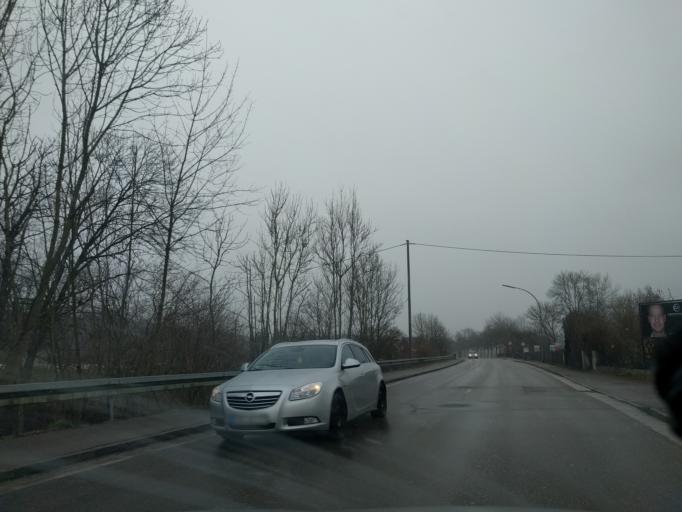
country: DE
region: Bavaria
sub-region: Swabia
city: Donauwoerth
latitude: 48.7042
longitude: 10.7948
